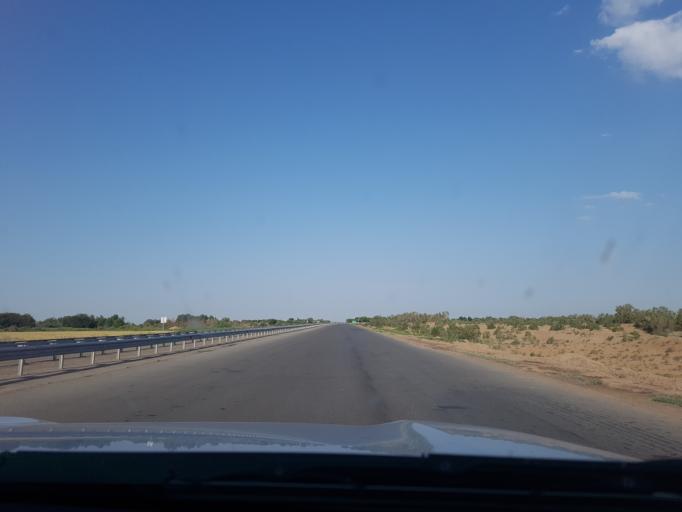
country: TM
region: Dasoguz
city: Yylanly
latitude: 41.7706
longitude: 59.4452
